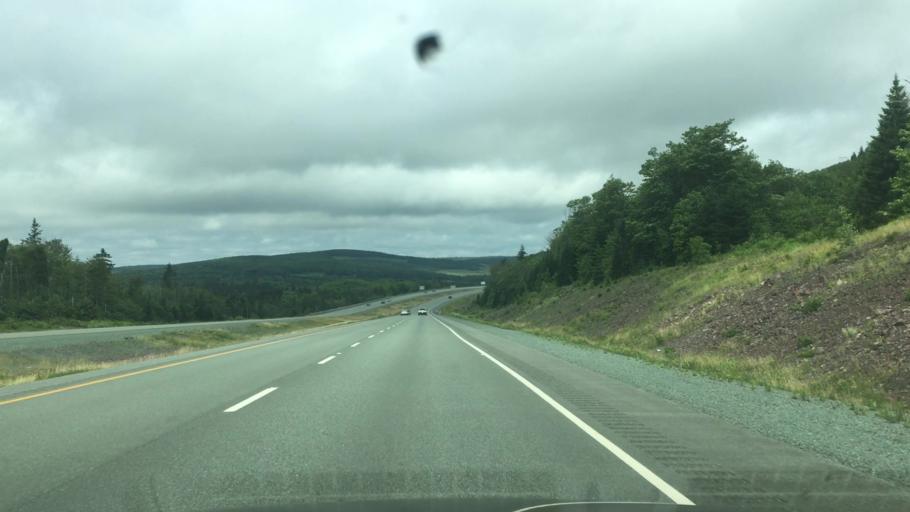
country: CA
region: Nova Scotia
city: Oxford
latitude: 45.5257
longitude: -63.7059
